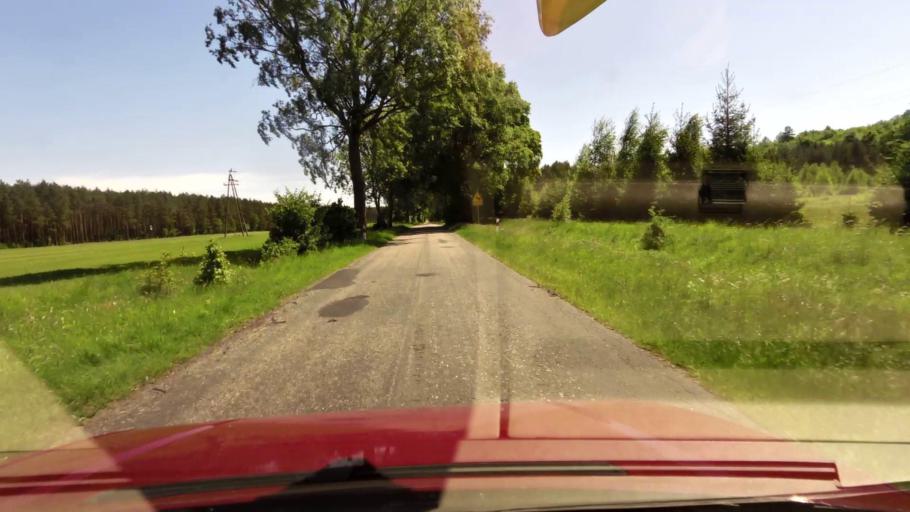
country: PL
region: West Pomeranian Voivodeship
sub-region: Powiat koszalinski
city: Bobolice
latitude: 54.0316
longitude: 16.6248
